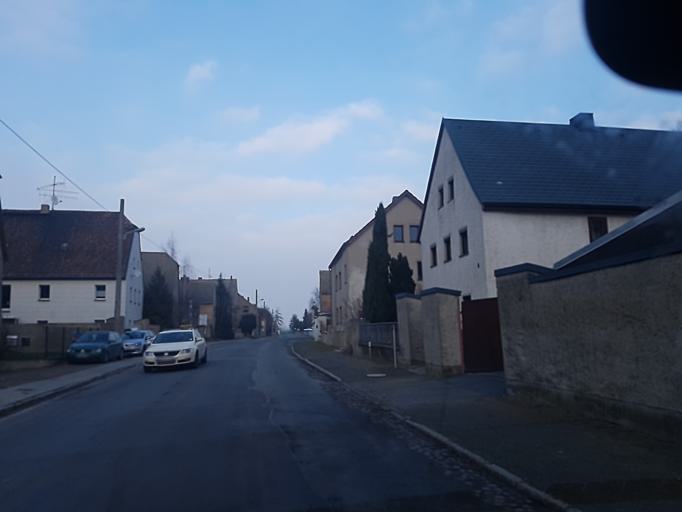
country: DE
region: Saxony
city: Oschatz
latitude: 51.3214
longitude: 13.0873
